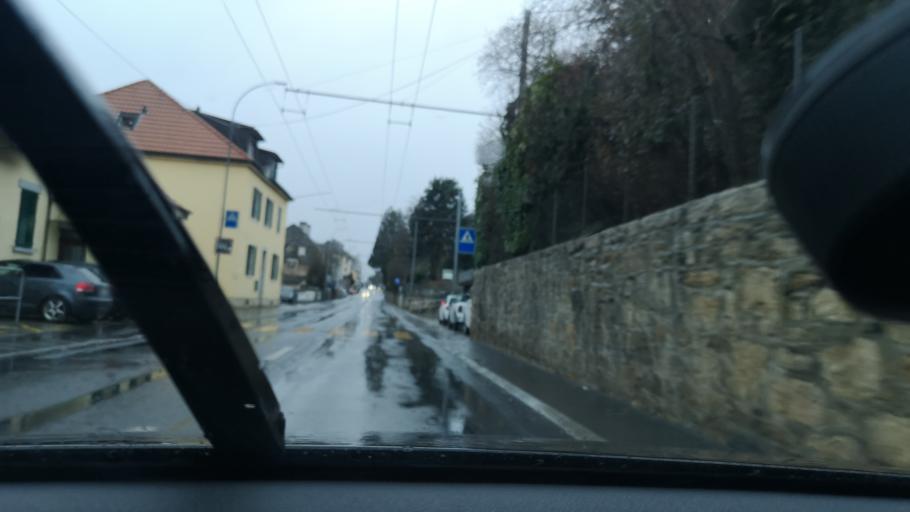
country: CH
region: Neuchatel
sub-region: Boudry District
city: Peseux
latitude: 46.9860
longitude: 6.8856
